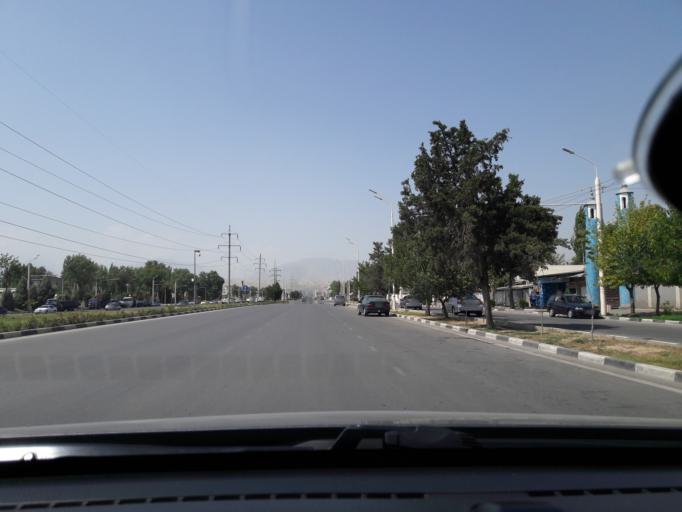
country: TJ
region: Dushanbe
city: Dushanbe
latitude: 38.5417
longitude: 68.7414
